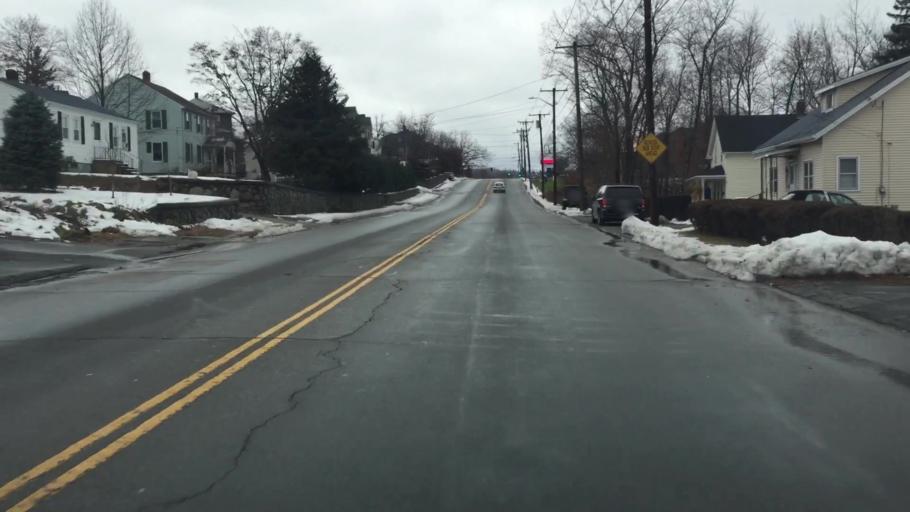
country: US
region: Massachusetts
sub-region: Worcester County
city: West Boylston
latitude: 42.3220
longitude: -71.7886
